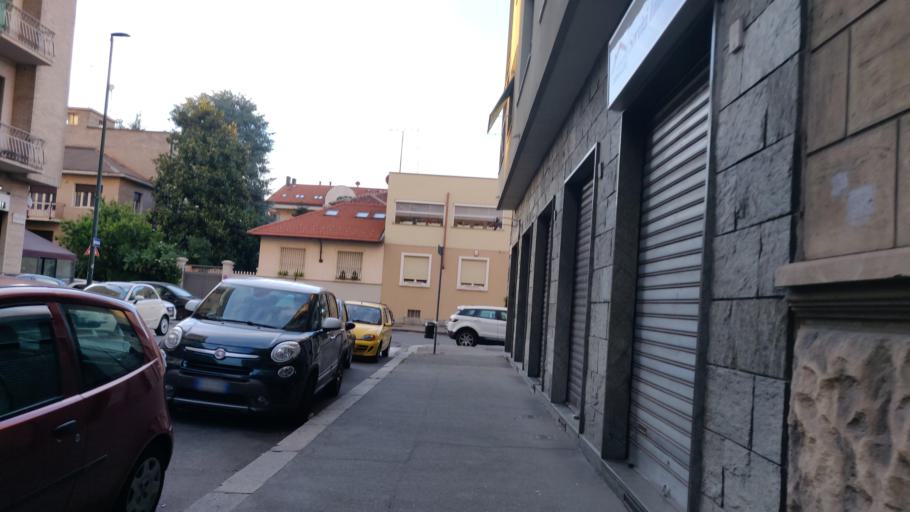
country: IT
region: Piedmont
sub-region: Provincia di Torino
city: Lesna
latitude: 45.0831
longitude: 7.6400
